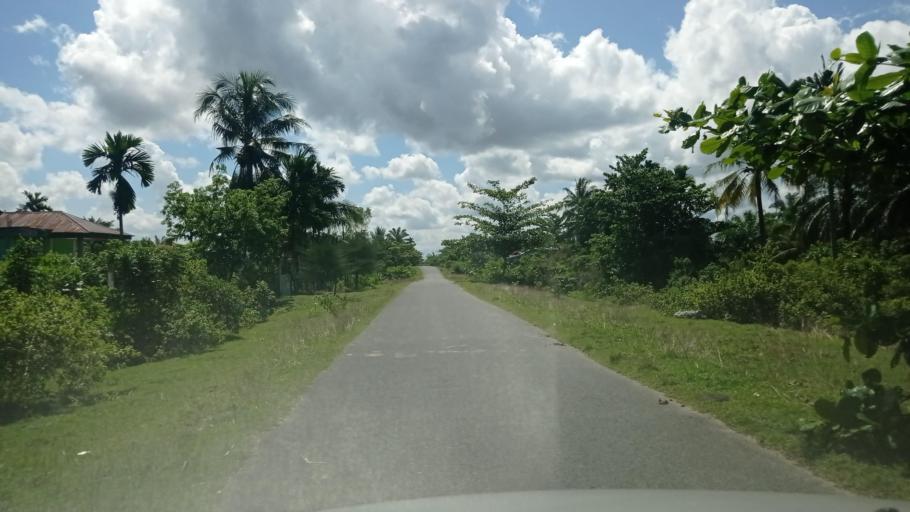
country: ID
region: Jambi
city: Sungai Penuh
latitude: -2.5514
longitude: 101.1019
